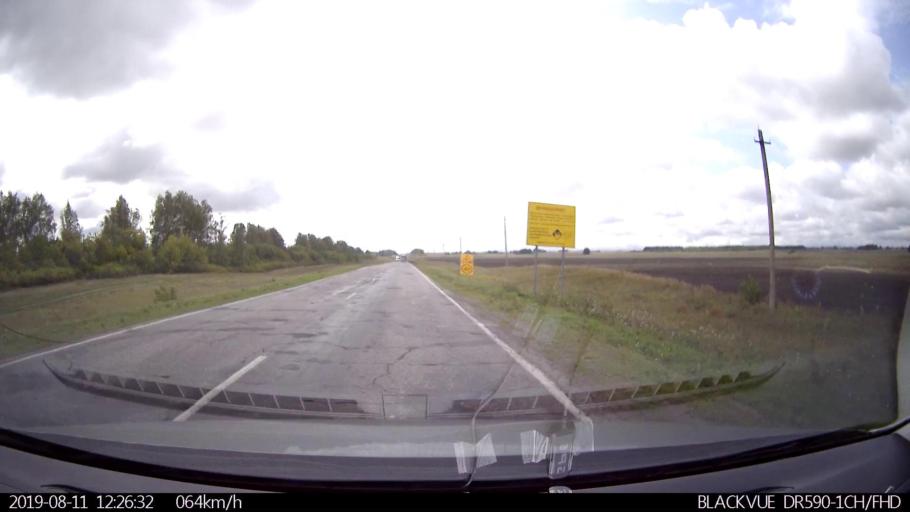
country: RU
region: Ulyanovsk
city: Ignatovka
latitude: 53.8631
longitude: 47.9296
